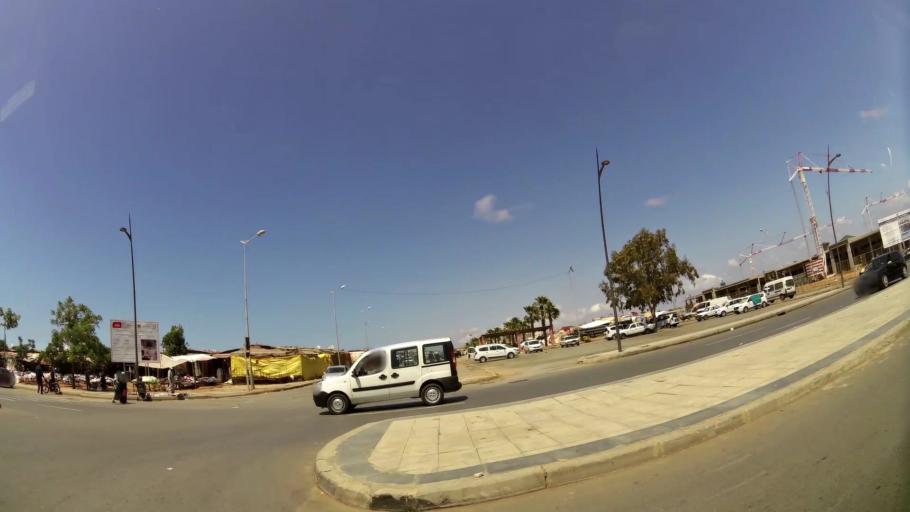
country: MA
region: Rabat-Sale-Zemmour-Zaer
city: Sale
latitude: 34.0472
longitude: -6.7924
